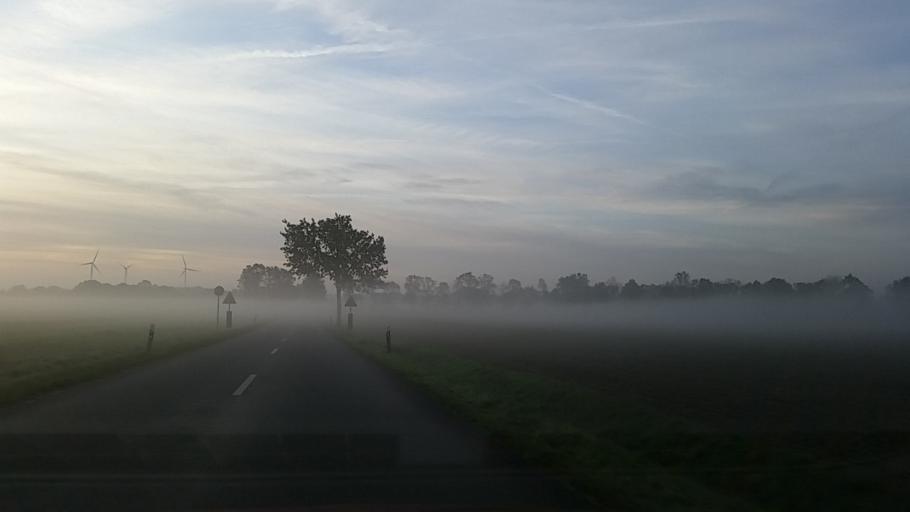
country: DE
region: Lower Saxony
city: Luder
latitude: 52.8039
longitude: 10.6938
